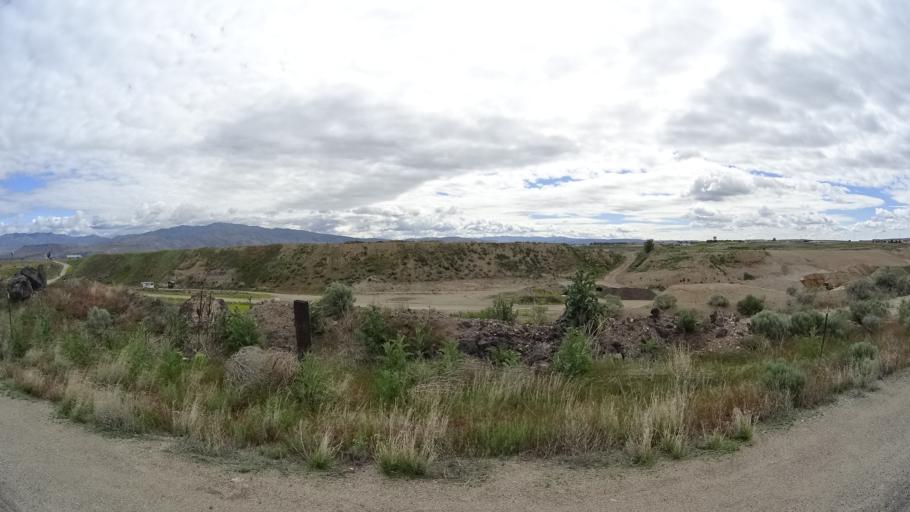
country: US
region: Idaho
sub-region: Ada County
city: Boise
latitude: 43.5536
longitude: -116.1869
